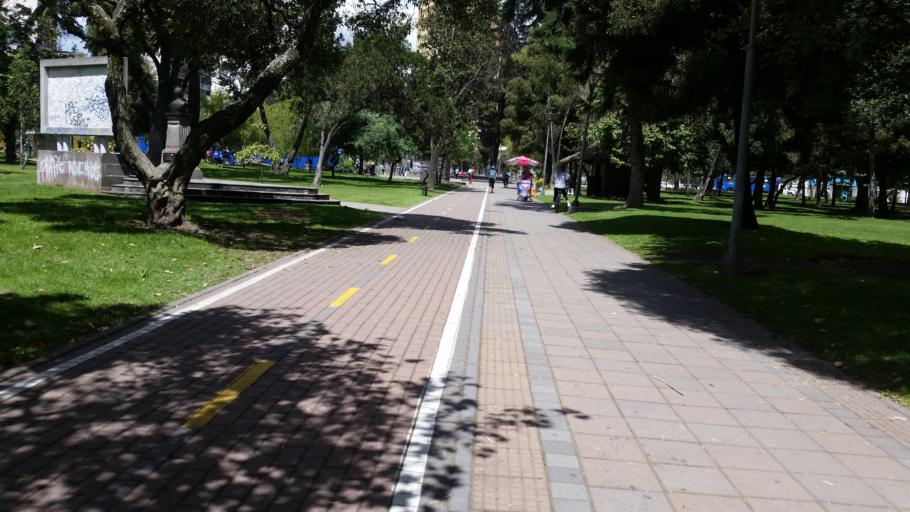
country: EC
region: Pichincha
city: Quito
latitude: -0.2103
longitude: -78.4998
